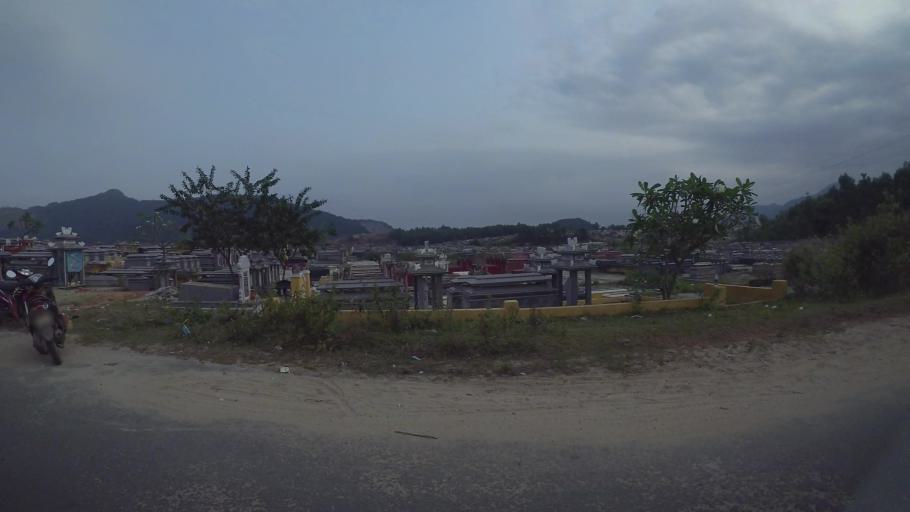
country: VN
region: Da Nang
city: Lien Chieu
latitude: 16.0618
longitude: 108.1109
